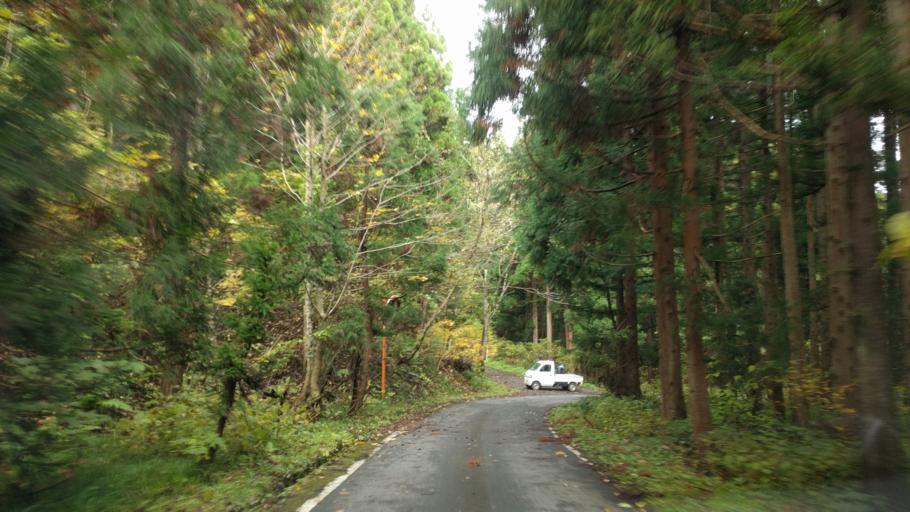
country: JP
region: Fukushima
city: Kitakata
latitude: 37.3841
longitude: 139.7040
